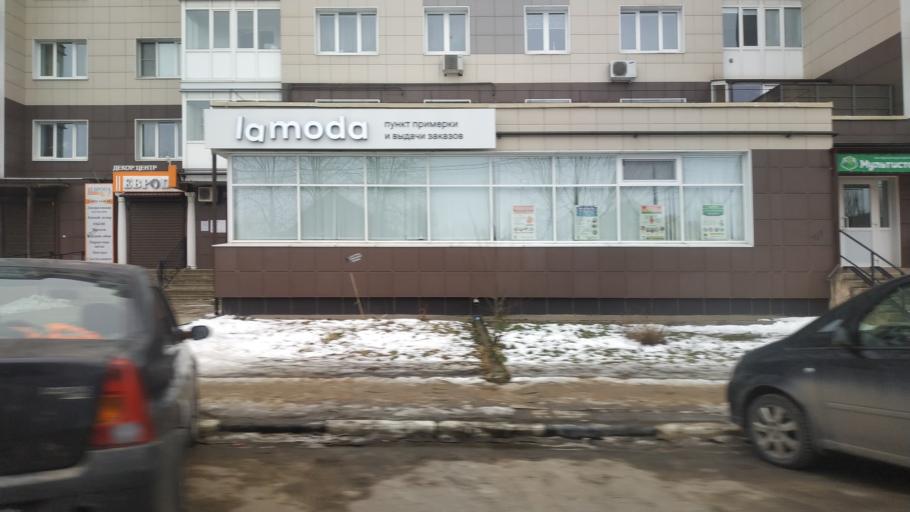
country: RU
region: Tverskaya
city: Tver
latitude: 56.8762
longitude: 35.8916
